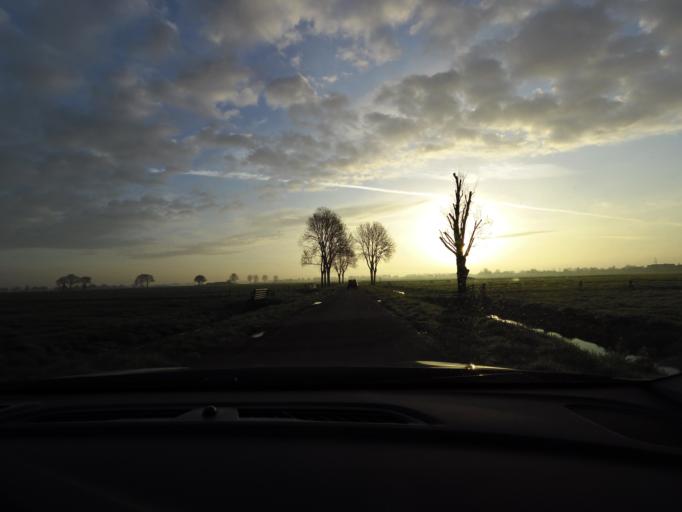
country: NL
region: South Holland
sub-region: Gemeente Giessenlanden
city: Giessenburg
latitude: 51.8553
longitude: 4.8751
